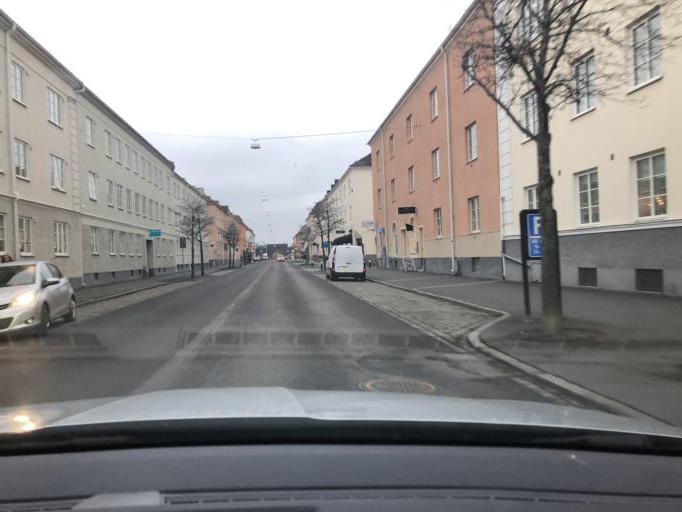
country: SE
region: Joenkoeping
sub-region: Jonkopings Kommun
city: Jonkoping
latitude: 57.7748
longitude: 14.1538
